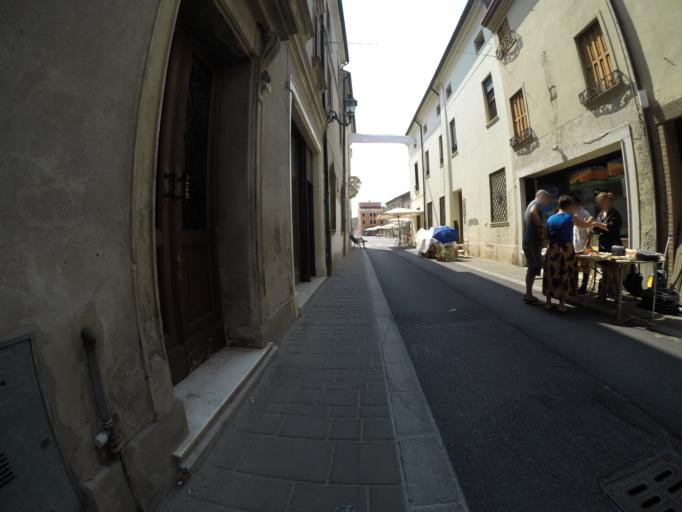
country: IT
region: Veneto
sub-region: Provincia di Rovigo
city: Lendinara
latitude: 45.0841
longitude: 11.5991
